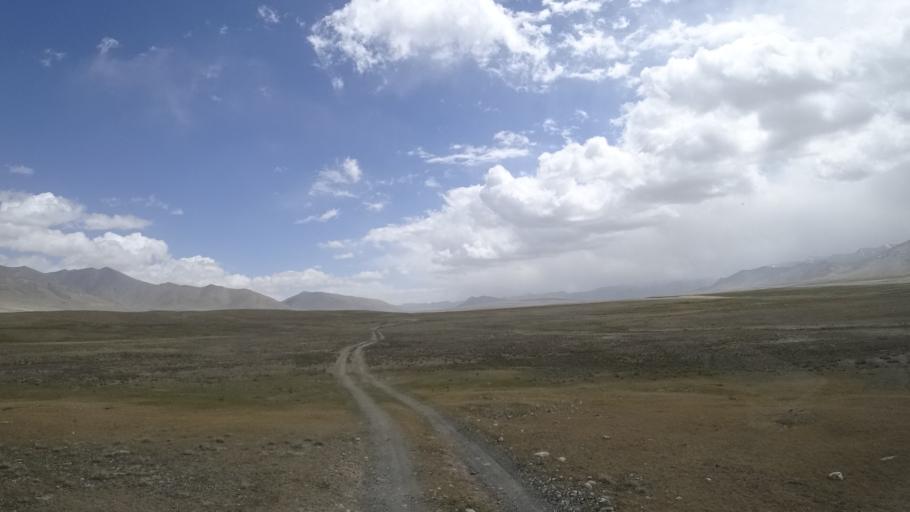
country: TJ
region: Gorno-Badakhshan
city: Murghob
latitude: 37.4723
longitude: 73.9654
